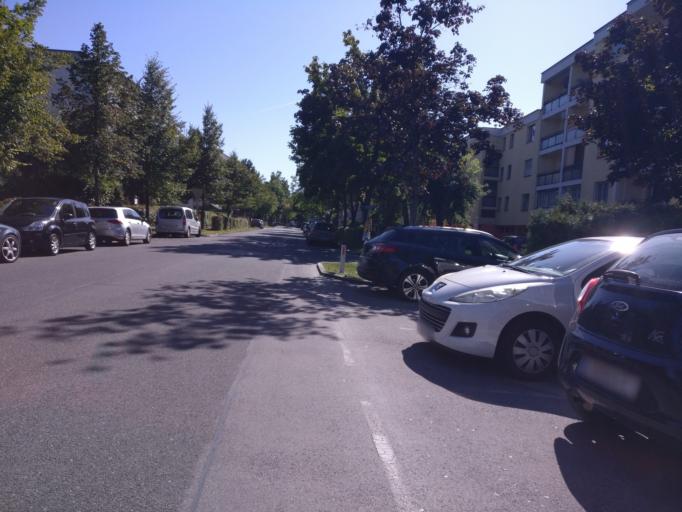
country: AT
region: Carinthia
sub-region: Klagenfurt am Woerthersee
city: Klagenfurt am Woerthersee
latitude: 46.6172
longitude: 14.2781
